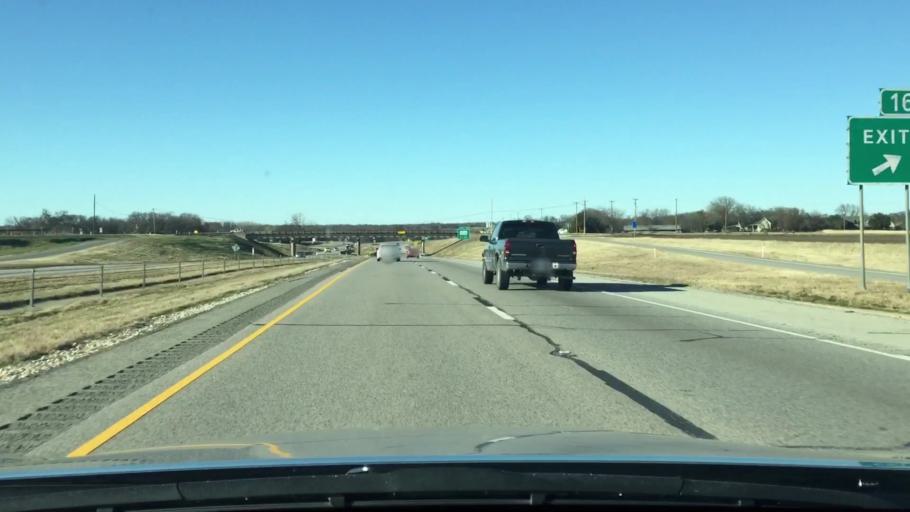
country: US
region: Texas
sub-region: Johnson County
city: Grandview
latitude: 32.2841
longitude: -97.1761
